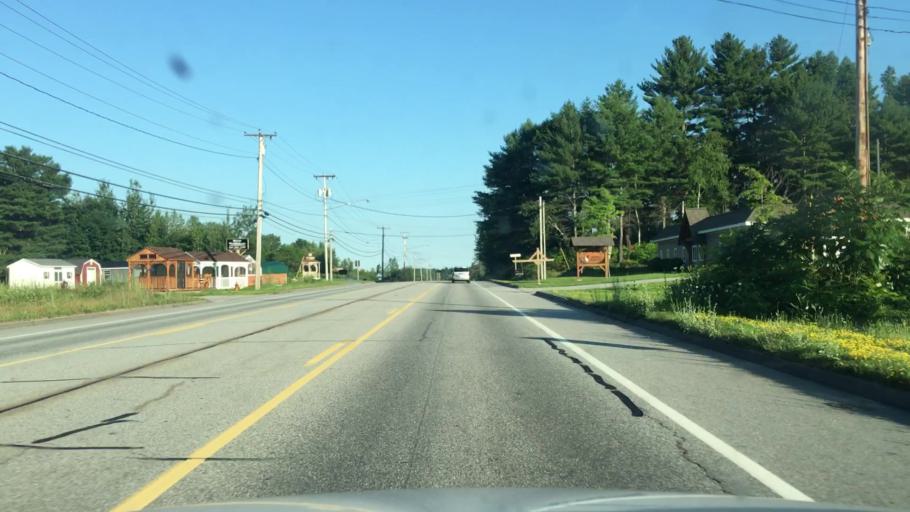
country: US
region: Maine
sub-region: Androscoggin County
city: Lisbon
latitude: 44.0595
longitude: -70.1454
